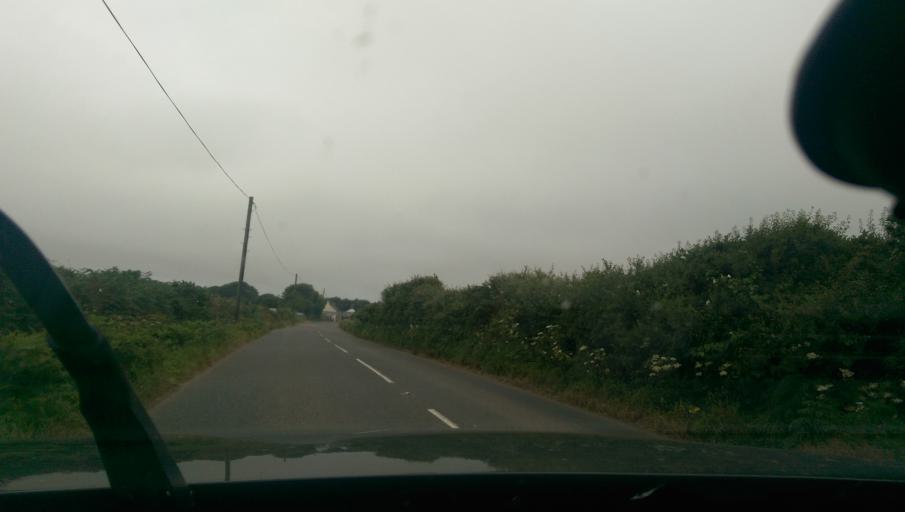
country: GB
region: England
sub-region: Cornwall
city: St. Buryan
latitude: 50.0912
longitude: -5.6396
